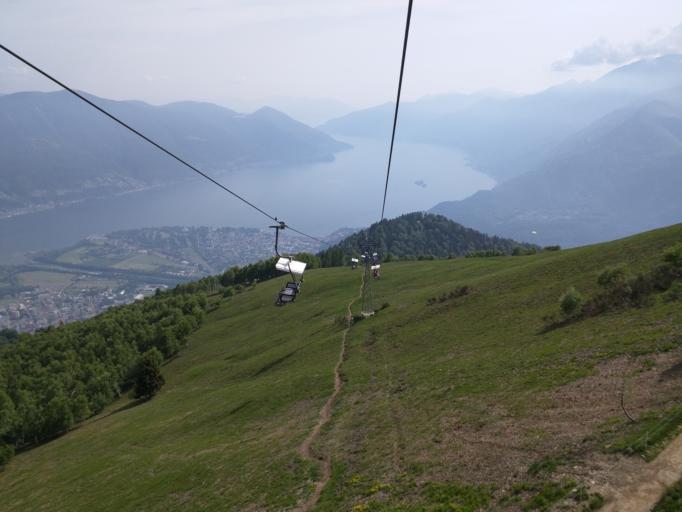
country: CH
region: Ticino
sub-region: Locarno District
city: Locarno
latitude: 46.1996
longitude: 8.7884
